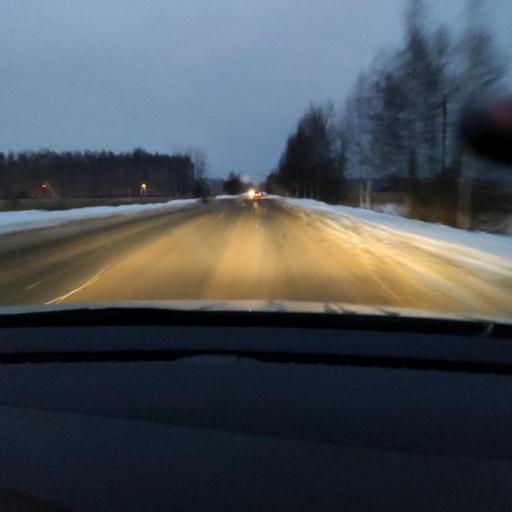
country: RU
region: Tatarstan
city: Aysha
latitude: 55.8625
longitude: 48.5845
